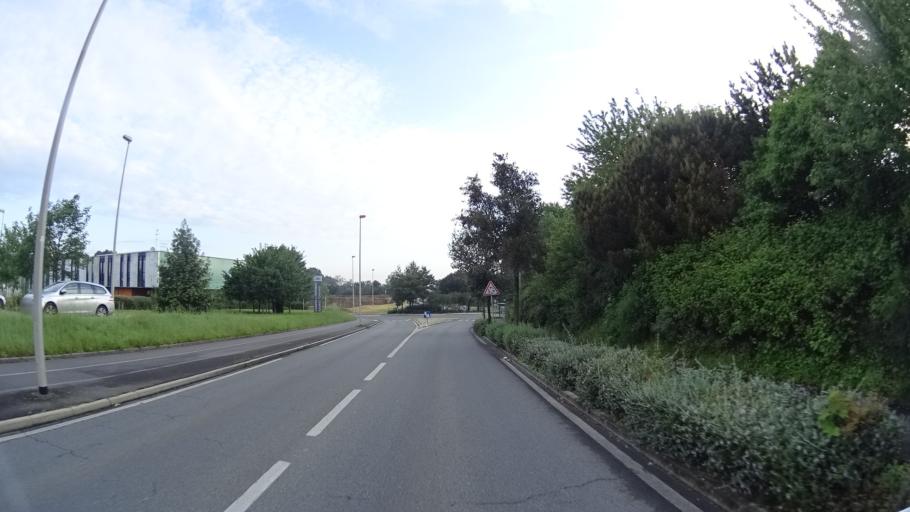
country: FR
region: Brittany
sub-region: Departement du Morbihan
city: Vannes
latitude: 47.6457
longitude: -2.7437
